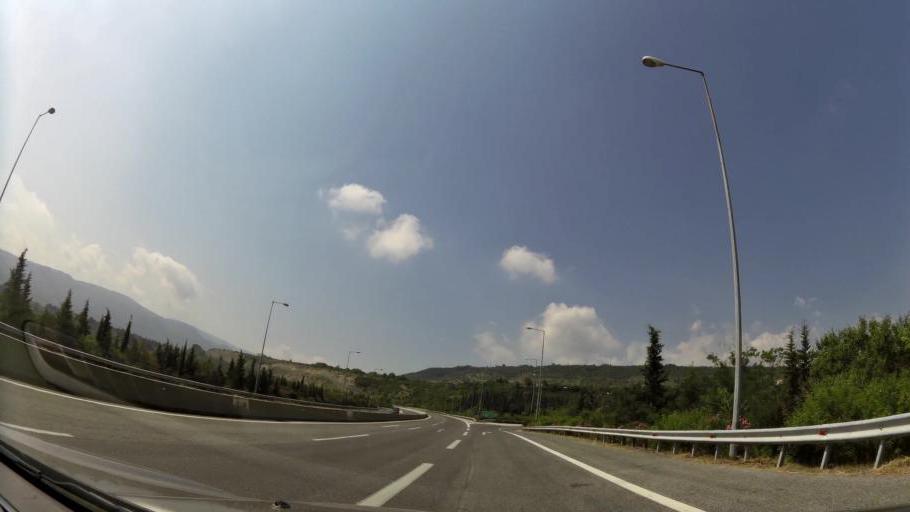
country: GR
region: Central Macedonia
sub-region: Nomos Imathias
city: Veroia
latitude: 40.5084
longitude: 22.2301
